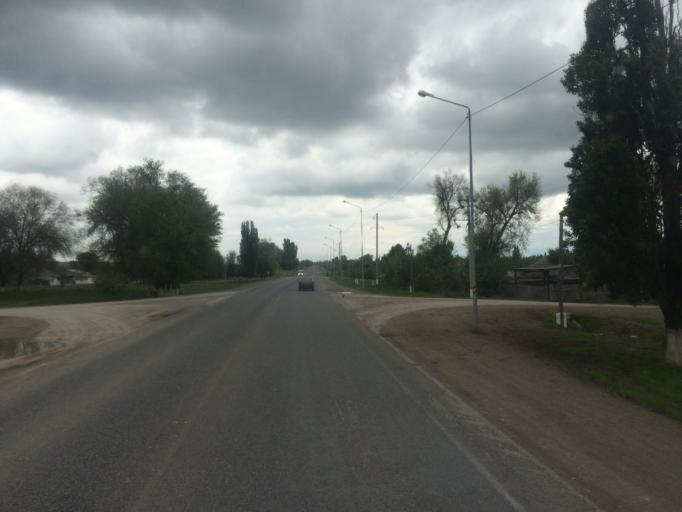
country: KZ
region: Zhambyl
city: Georgiyevka
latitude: 43.1404
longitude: 74.6196
